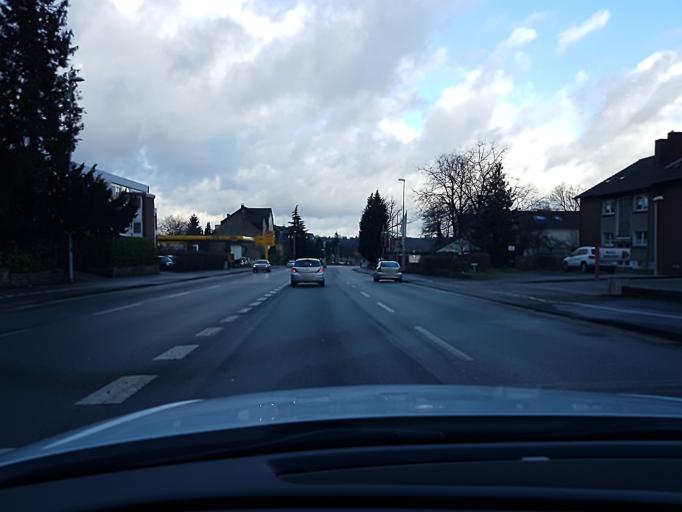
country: DE
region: North Rhine-Westphalia
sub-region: Regierungsbezirk Dusseldorf
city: Muelheim (Ruhr)
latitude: 51.3980
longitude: 6.8755
